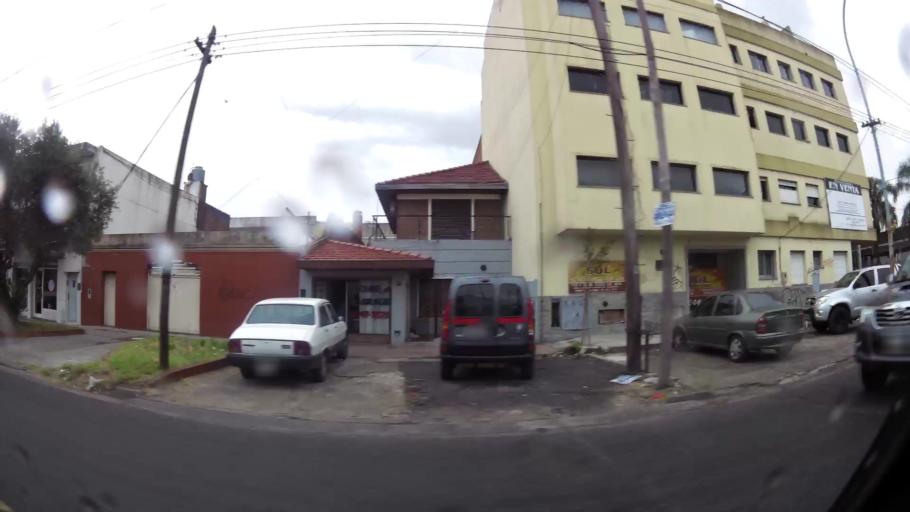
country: AR
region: Buenos Aires
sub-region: Partido de Lanus
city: Lanus
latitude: -34.6991
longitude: -58.4043
